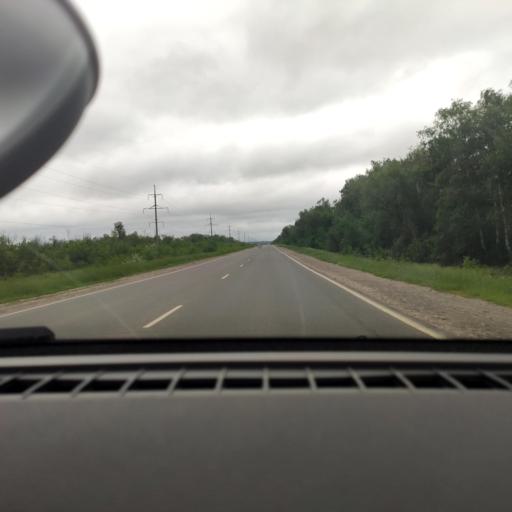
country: RU
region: Samara
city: Dubovyy Umet
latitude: 53.1028
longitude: 50.2523
